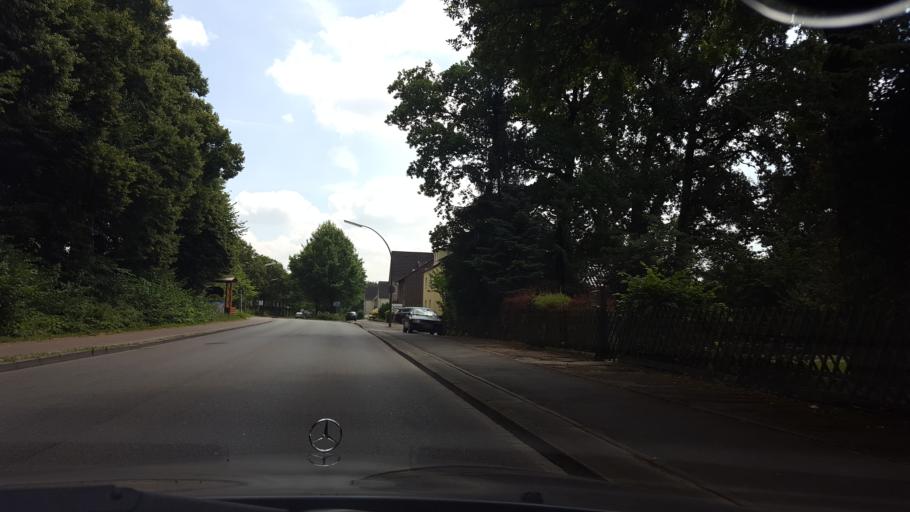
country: DE
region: North Rhine-Westphalia
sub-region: Regierungsbezirk Munster
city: Recklinghausen
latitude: 51.6638
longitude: 7.1744
